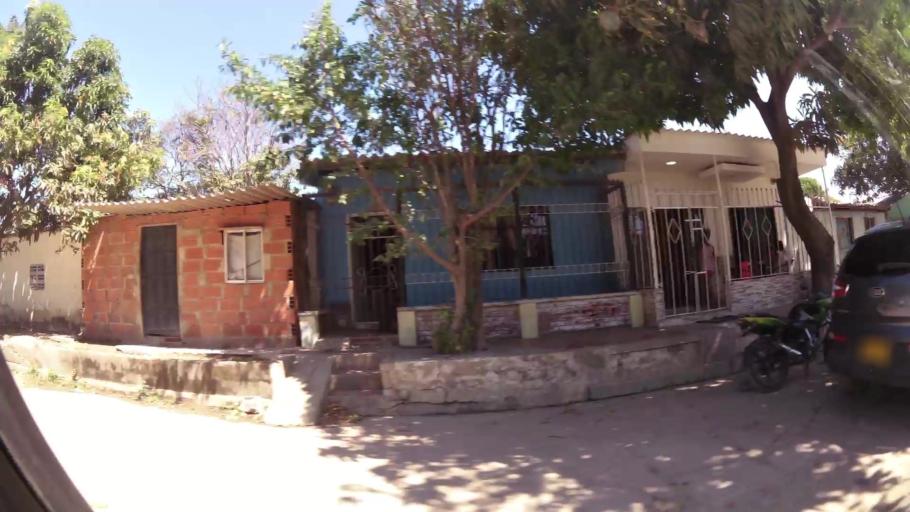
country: CO
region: Atlantico
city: Barranquilla
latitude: 10.9809
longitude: -74.7669
